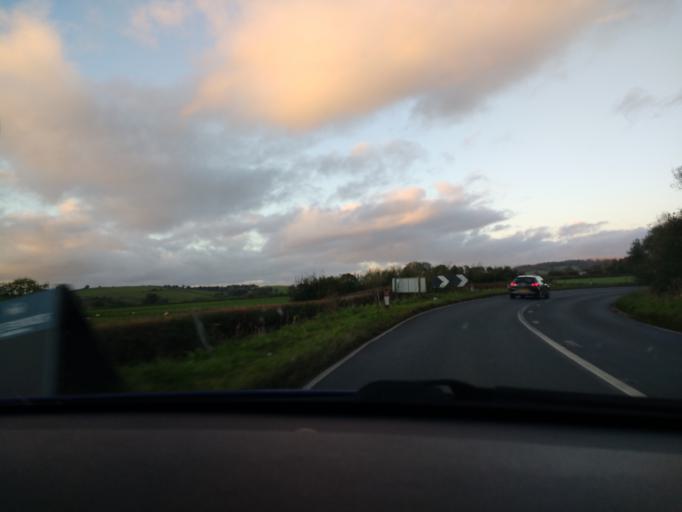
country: GB
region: England
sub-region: Lancashire
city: Caton
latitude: 54.0958
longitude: -2.6625
